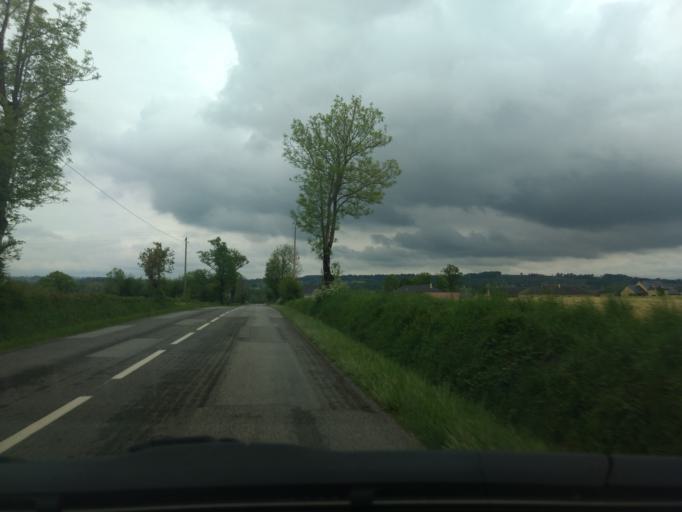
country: FR
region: Midi-Pyrenees
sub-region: Departement de l'Aveyron
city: Montbazens
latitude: 44.4286
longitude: 2.2647
